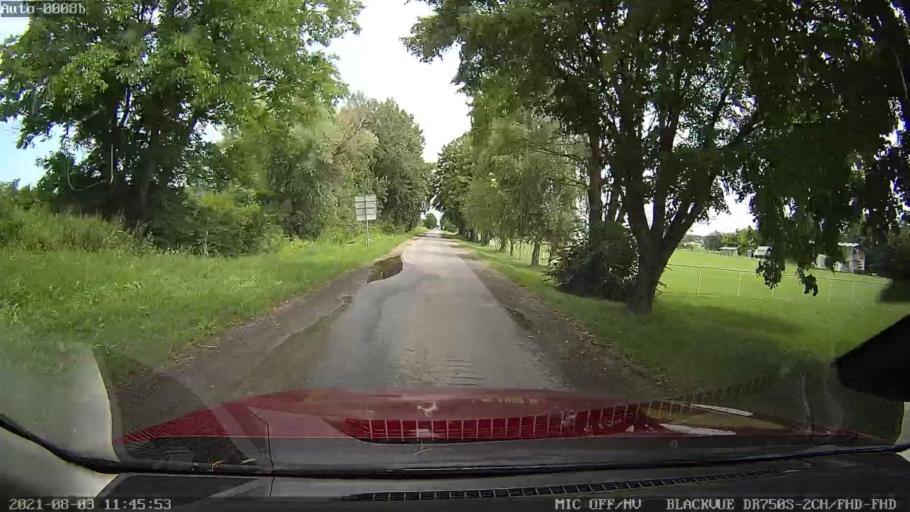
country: HR
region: Osjecko-Baranjska
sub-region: Grad Osijek
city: Bilje
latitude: 45.6036
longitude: 18.7839
